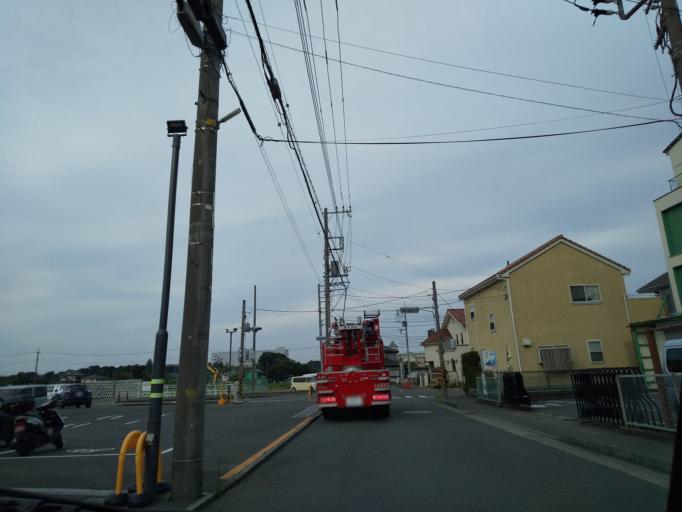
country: JP
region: Kanagawa
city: Atsugi
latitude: 35.4694
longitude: 139.3585
